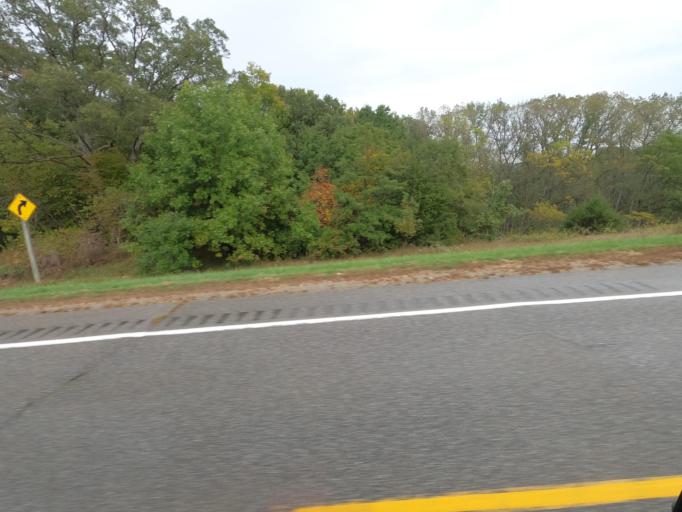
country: US
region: Iowa
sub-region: Van Buren County
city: Keosauqua
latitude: 40.8203
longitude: -91.9449
